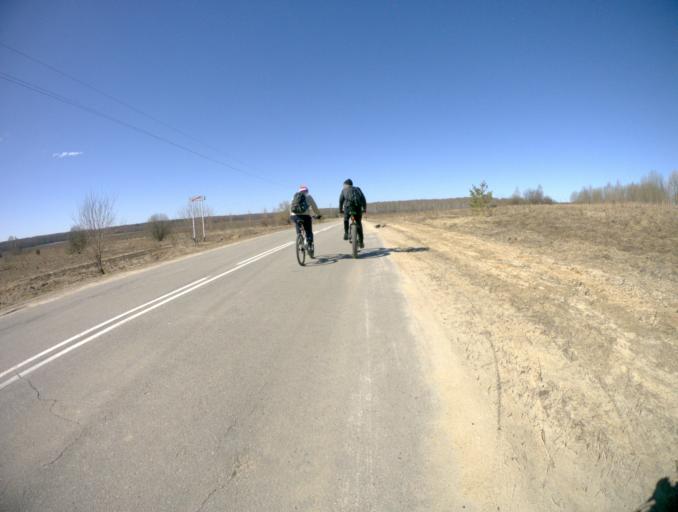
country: RU
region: Vladimir
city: Kameshkovo
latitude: 56.3472
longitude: 40.8000
